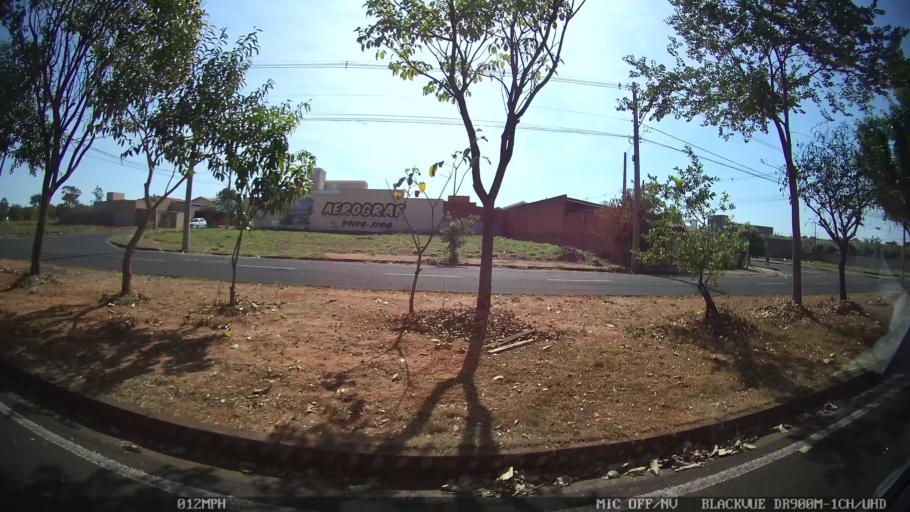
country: BR
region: Sao Paulo
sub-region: Sao Jose Do Rio Preto
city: Sao Jose do Rio Preto
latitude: -20.7928
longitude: -49.4413
